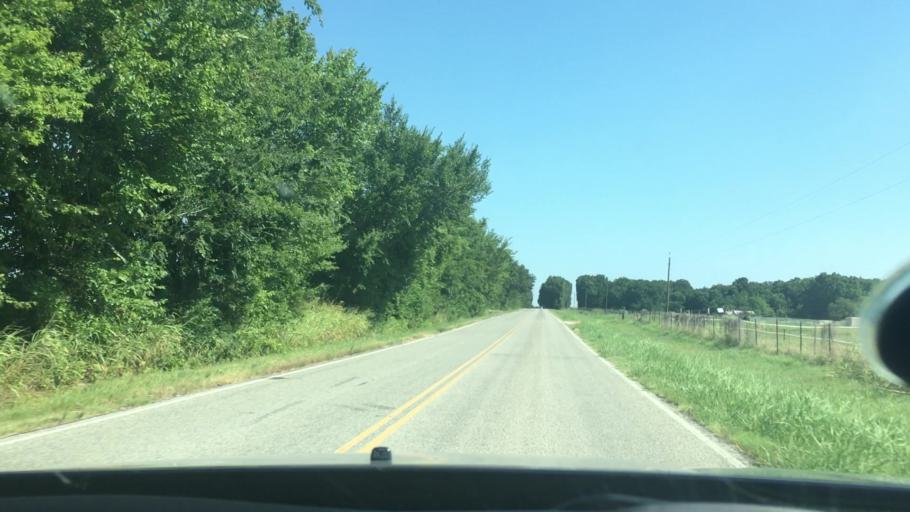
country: US
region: Oklahoma
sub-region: Johnston County
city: Tishomingo
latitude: 34.2923
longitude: -96.6185
